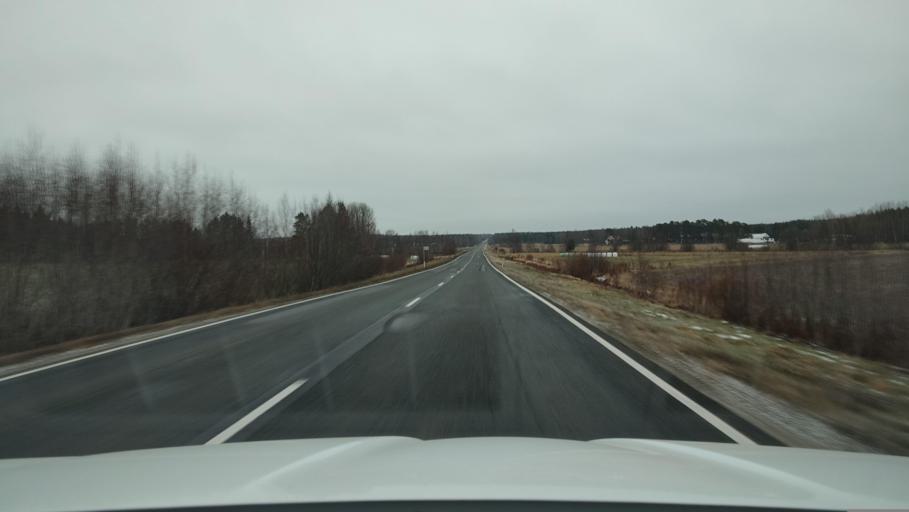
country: FI
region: Ostrobothnia
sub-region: Sydosterbotten
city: Naerpes
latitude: 62.4011
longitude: 21.3746
